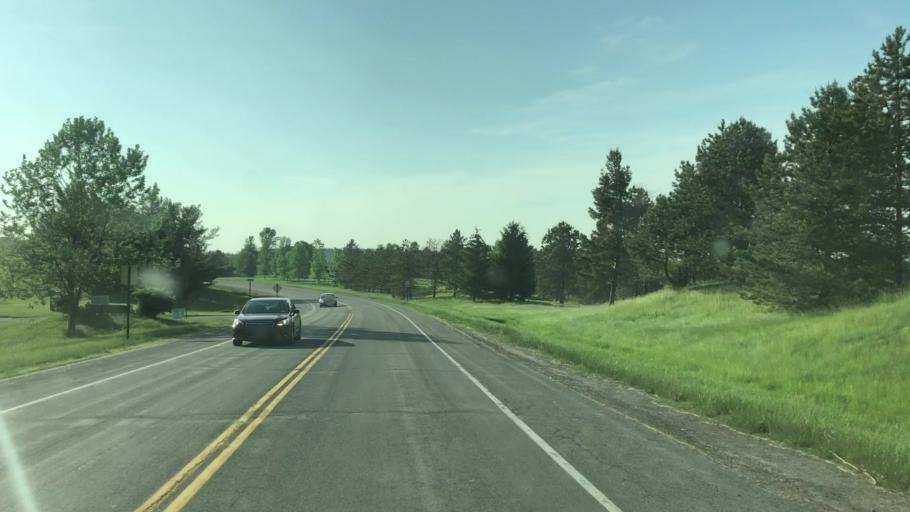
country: US
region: New York
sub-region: Wayne County
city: Macedon
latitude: 43.1207
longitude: -77.3148
